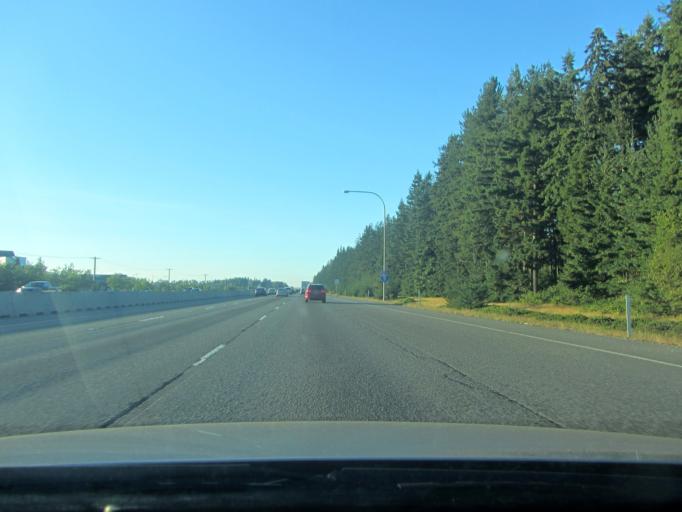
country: US
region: Washington
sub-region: Snohomish County
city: Marysville
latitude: 48.0800
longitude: -122.1846
